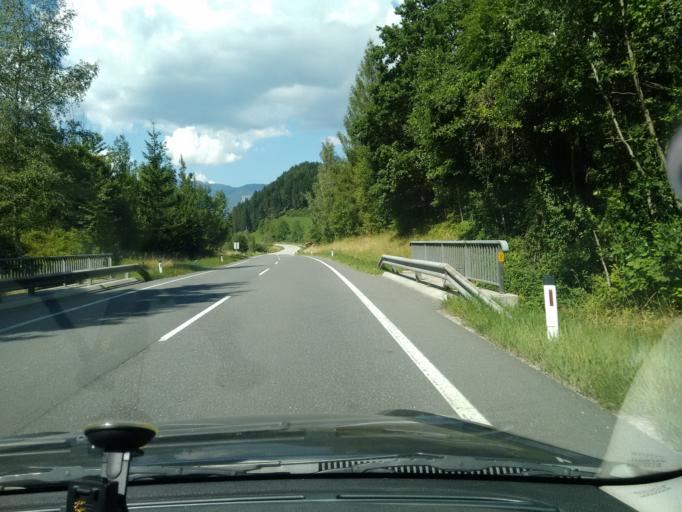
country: AT
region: Upper Austria
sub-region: Politischer Bezirk Kirchdorf an der Krems
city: Rossleithen
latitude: 47.6738
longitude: 14.3497
